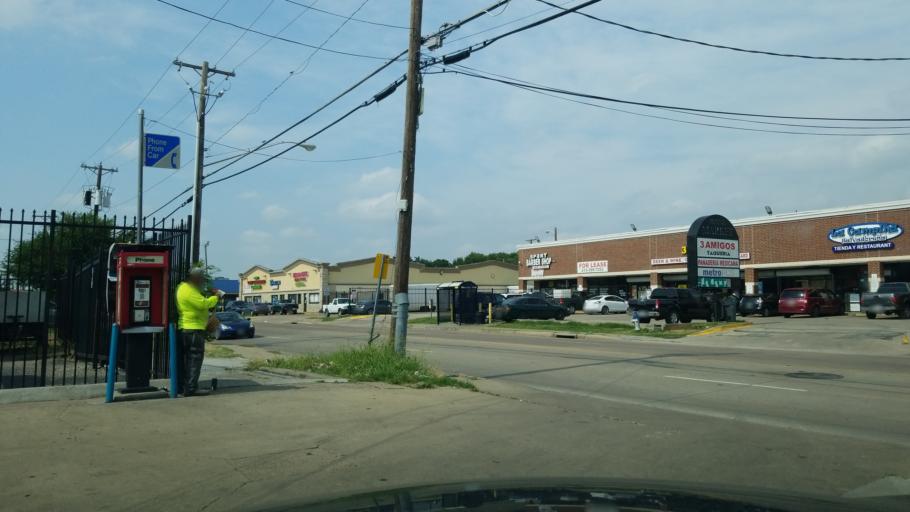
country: US
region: Texas
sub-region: Dallas County
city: Farmers Branch
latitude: 32.8956
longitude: -96.8816
